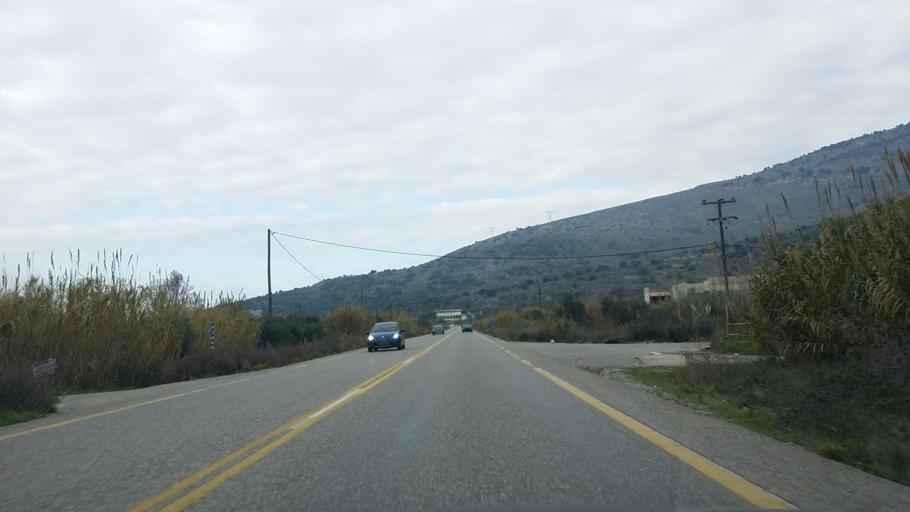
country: GR
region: West Greece
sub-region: Nomos Aitolias kai Akarnanias
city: Mesolongi
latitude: 38.4058
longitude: 21.4023
